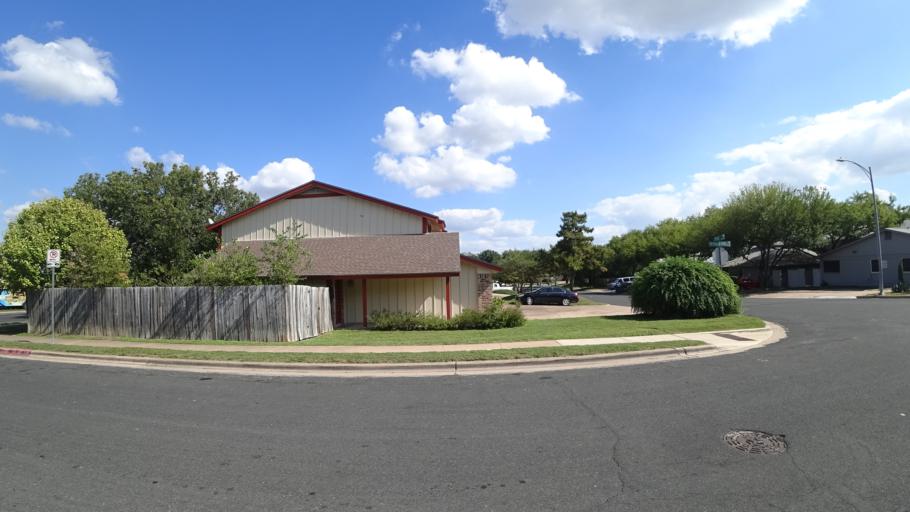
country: US
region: Texas
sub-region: Travis County
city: Wells Branch
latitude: 30.3643
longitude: -97.7106
